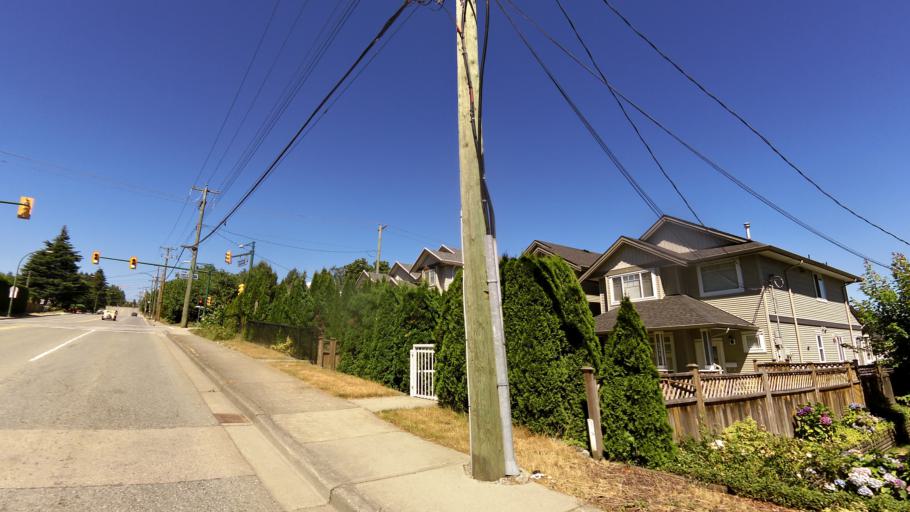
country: CA
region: British Columbia
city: Port Moody
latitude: 49.2392
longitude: -122.8730
